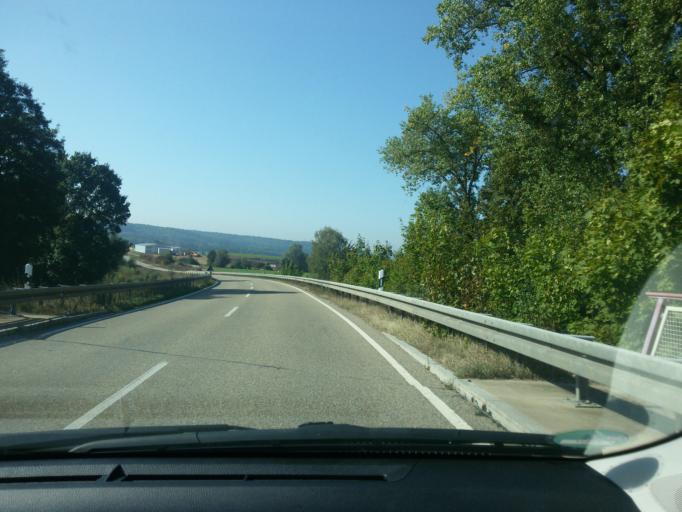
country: DE
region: Bavaria
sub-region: Regierungsbezirk Mittelfranken
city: Wassertrudingen
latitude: 49.0510
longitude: 10.5879
